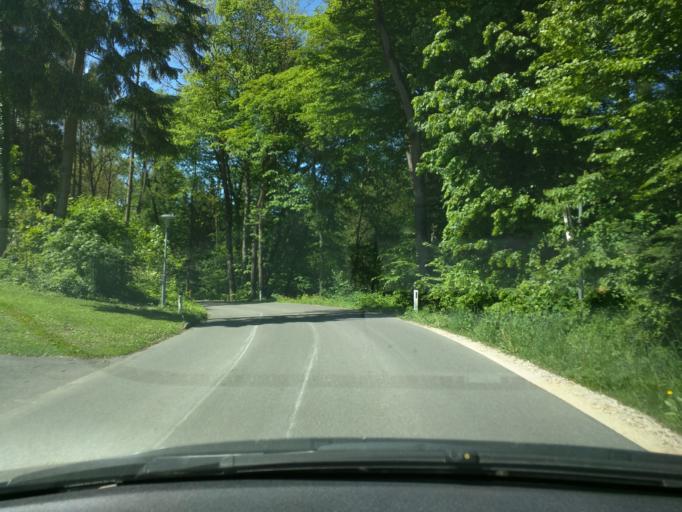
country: AT
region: Lower Austria
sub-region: Politischer Bezirk Amstetten
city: Sankt Georgen am Ybbsfelde
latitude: 48.1324
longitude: 14.9234
